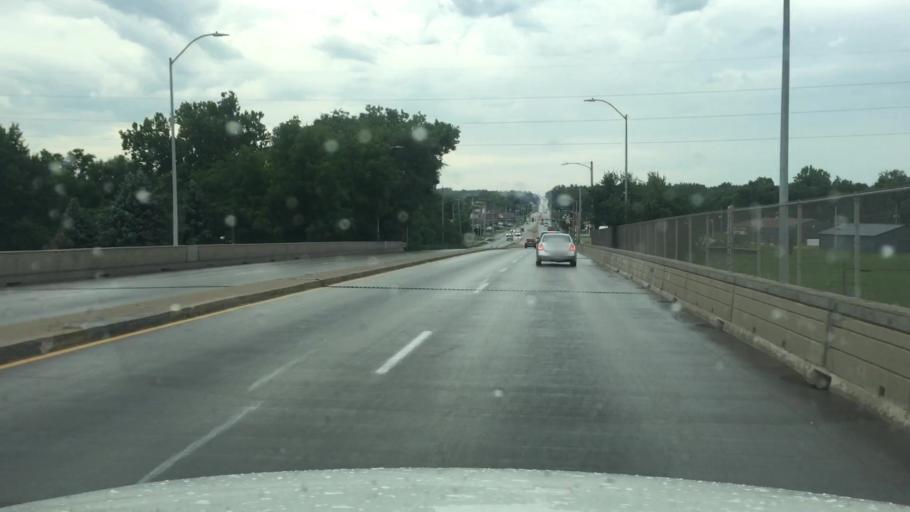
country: US
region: Iowa
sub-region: Polk County
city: Des Moines
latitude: 41.5841
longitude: -93.5970
